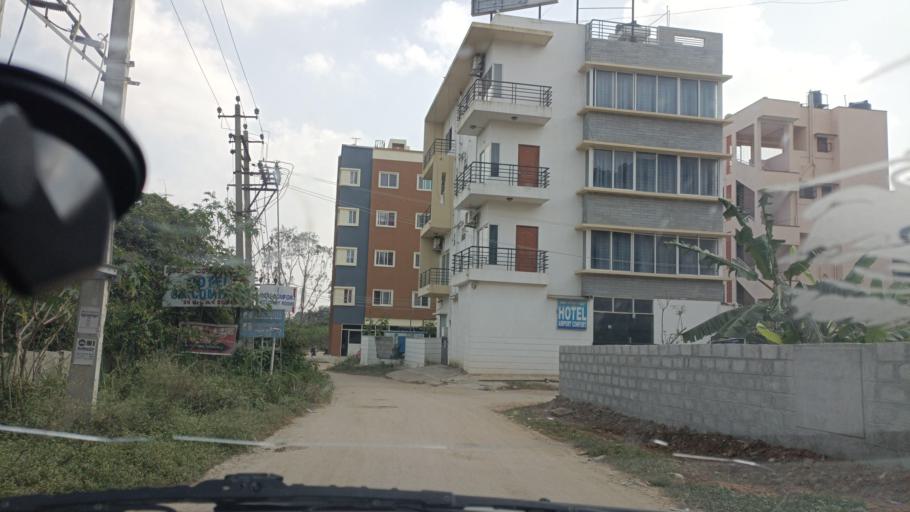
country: IN
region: Karnataka
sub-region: Bangalore Urban
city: Yelahanka
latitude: 13.1481
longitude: 77.6200
